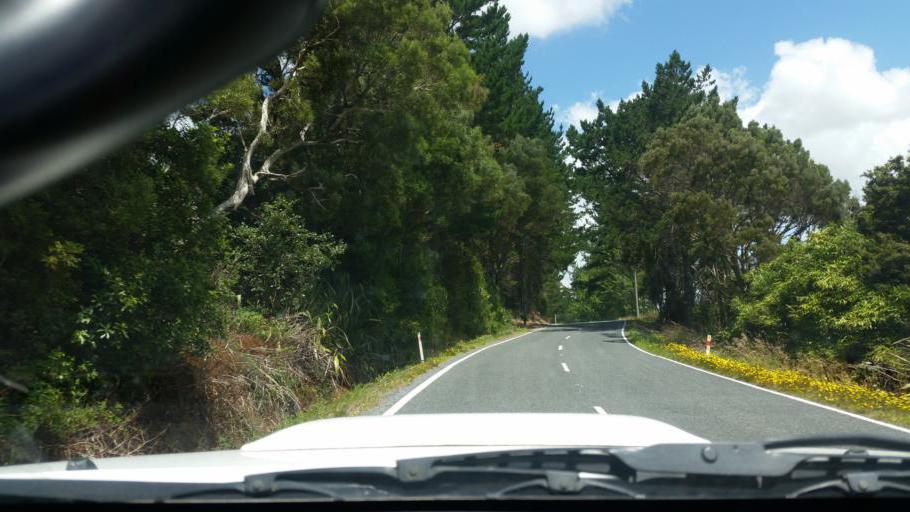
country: NZ
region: Northland
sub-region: Whangarei
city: Ruakaka
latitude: -36.0682
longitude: 174.2655
